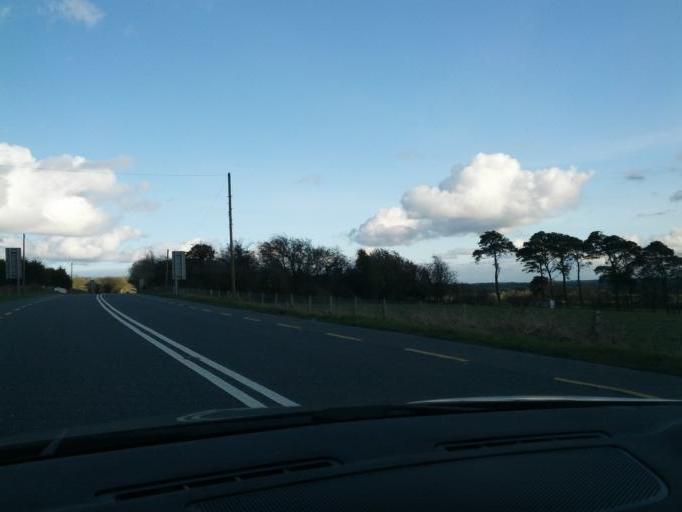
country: IE
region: Connaught
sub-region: Roscommon
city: Castlerea
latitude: 53.6855
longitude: -8.3635
